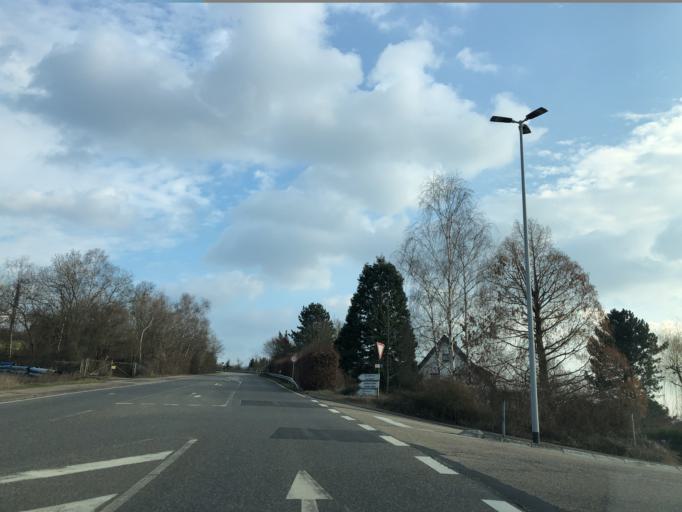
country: DE
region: Rheinland-Pfalz
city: Lahnstein
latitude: 50.3028
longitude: 7.6216
